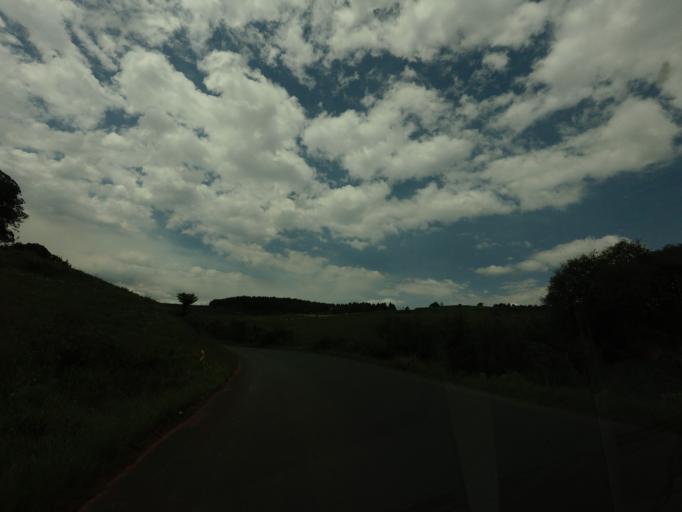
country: ZA
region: Mpumalanga
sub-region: Ehlanzeni District
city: Graksop
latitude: -24.9944
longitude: 30.8135
